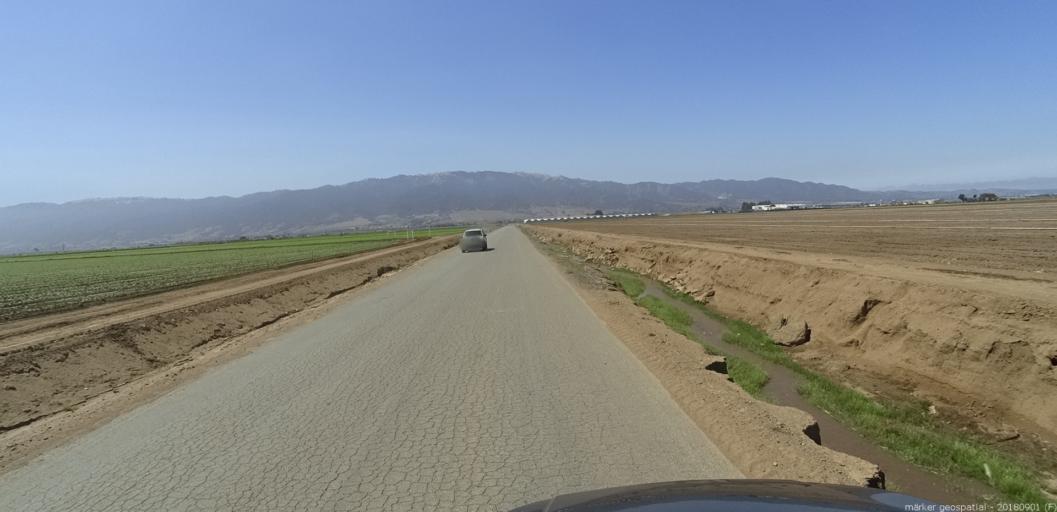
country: US
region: California
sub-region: Monterey County
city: Chualar
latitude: 36.5967
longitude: -121.5253
